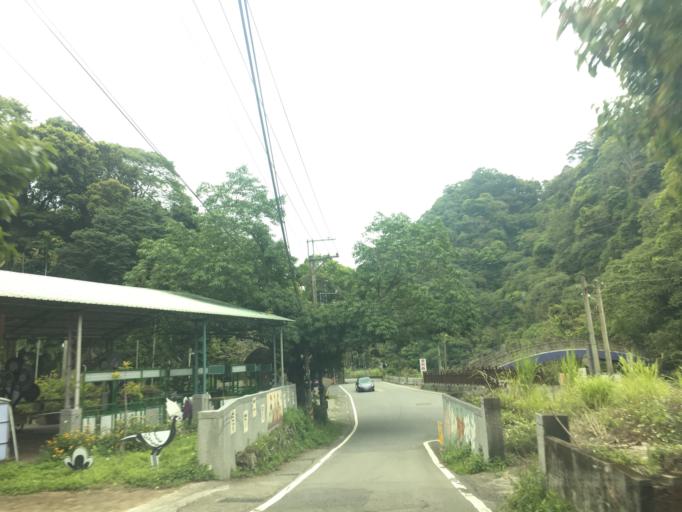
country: TW
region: Taiwan
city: Fengyuan
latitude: 24.1594
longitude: 120.8265
